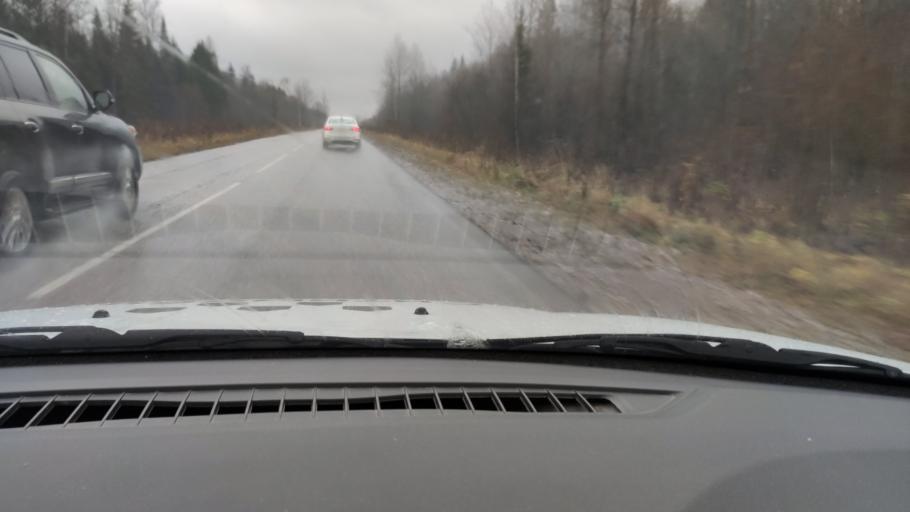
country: RU
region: Perm
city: Novyye Lyady
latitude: 58.0347
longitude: 56.6059
